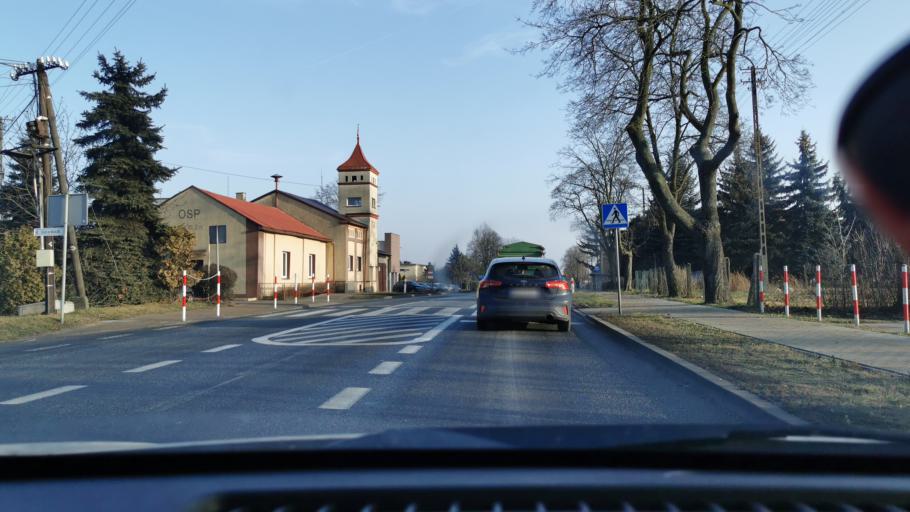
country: PL
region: Lodz Voivodeship
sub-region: Powiat sieradzki
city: Wroblew
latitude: 51.6118
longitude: 18.6159
